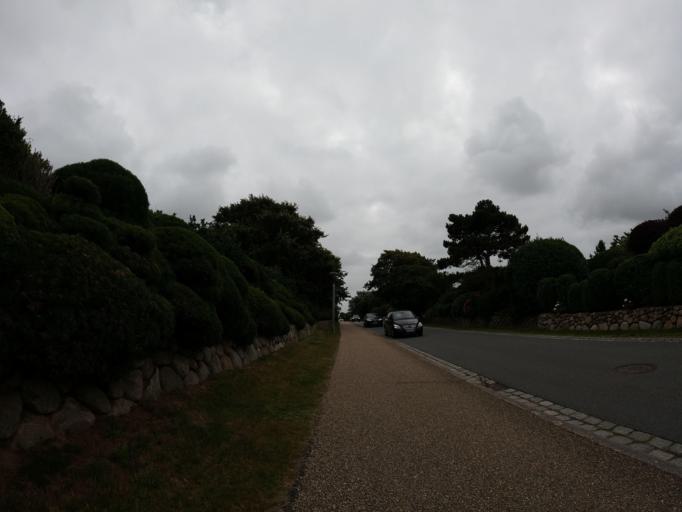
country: DE
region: Schleswig-Holstein
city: Tinnum
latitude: 54.9517
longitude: 8.3443
